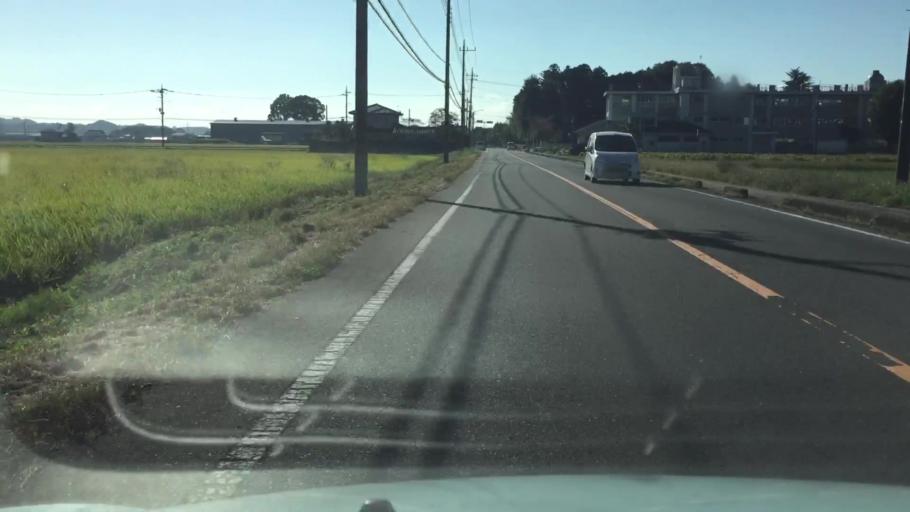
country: JP
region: Tochigi
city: Ujiie
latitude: 36.6868
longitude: 140.0040
